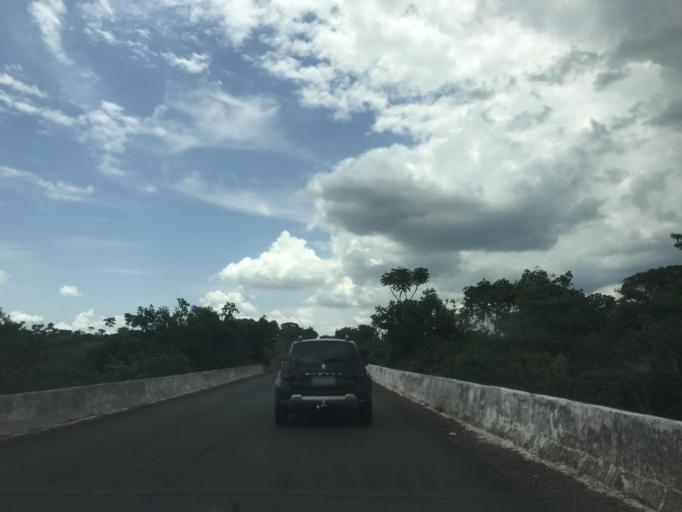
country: BR
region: Goias
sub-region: Vianopolis
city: Vianopolis
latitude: -16.9471
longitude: -48.5813
